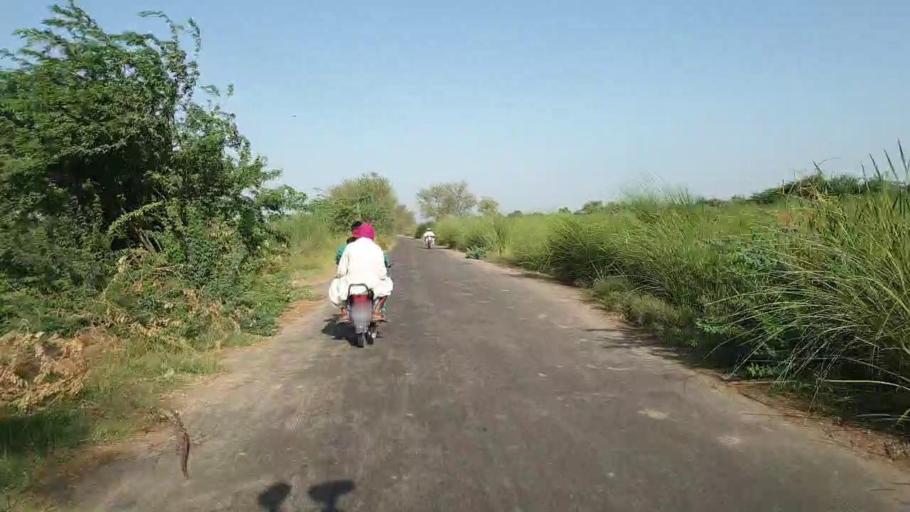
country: PK
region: Sindh
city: Nawabshah
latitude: 26.3741
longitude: 68.4677
